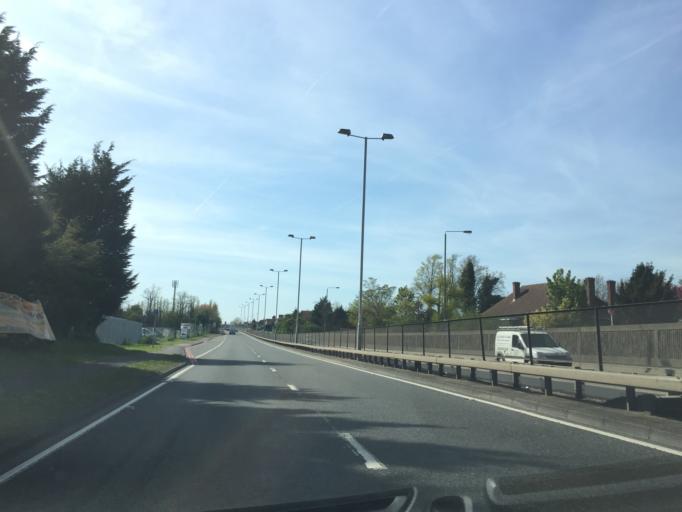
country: GB
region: England
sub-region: Greater London
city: Chislehurst
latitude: 51.4305
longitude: 0.0821
